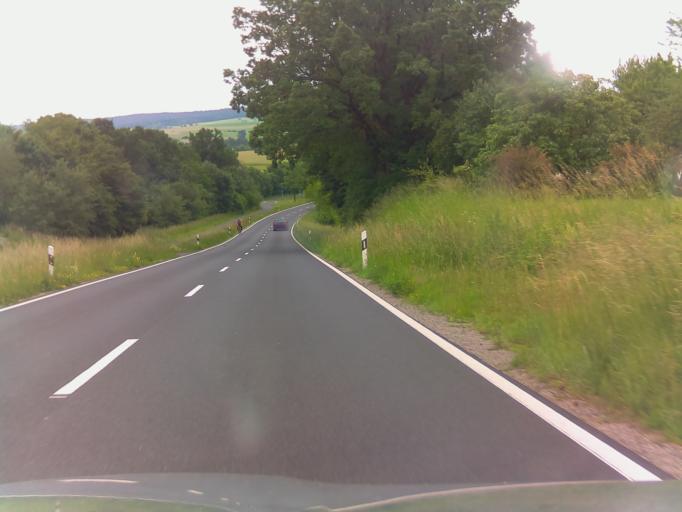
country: DE
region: Bavaria
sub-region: Regierungsbezirk Unterfranken
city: Oberleichtersbach
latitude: 50.2749
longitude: 9.8081
